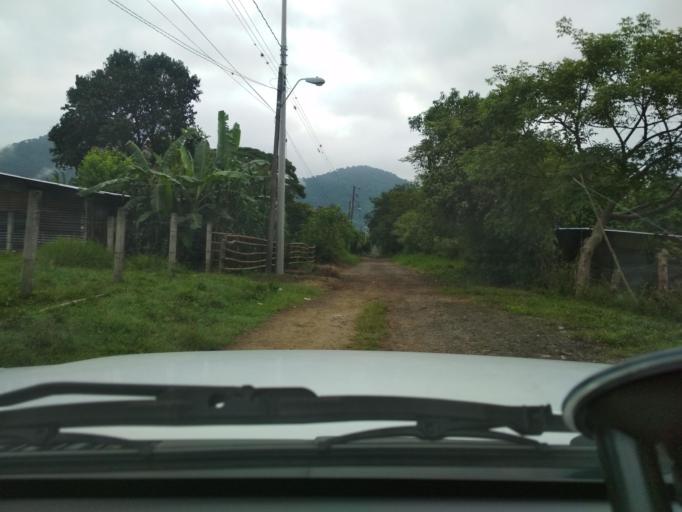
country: MX
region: Veracruz
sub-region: Ixtaczoquitlan
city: Buenavista
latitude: 18.9132
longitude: -97.0508
